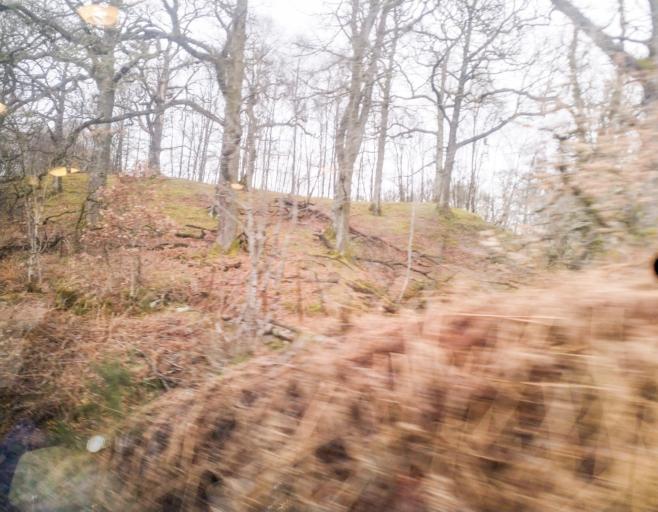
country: GB
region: Scotland
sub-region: Highland
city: Spean Bridge
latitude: 56.8933
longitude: -4.8906
